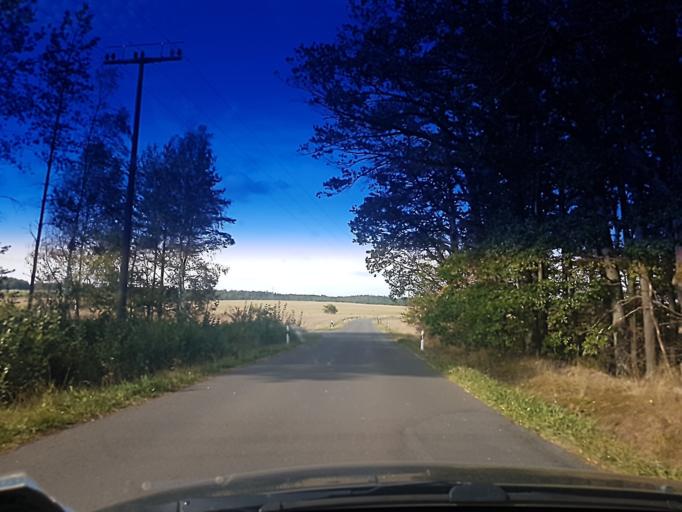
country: DE
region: Bavaria
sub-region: Upper Franconia
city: Schlusselfeld
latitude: 49.7839
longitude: 10.5841
